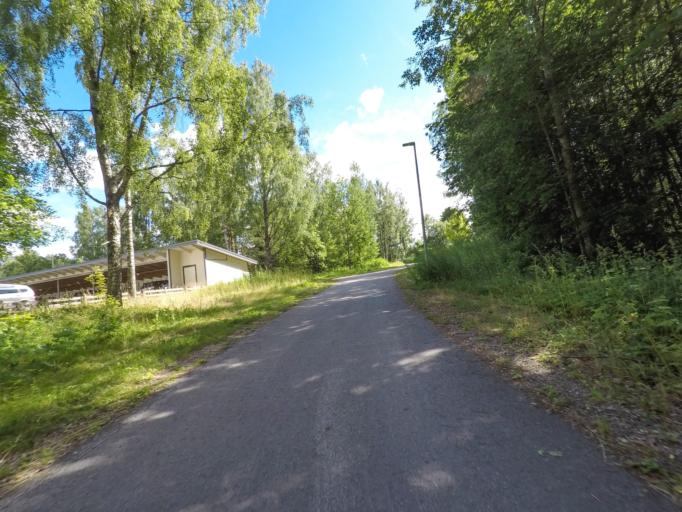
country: FI
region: South Karelia
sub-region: Lappeenranta
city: Lappeenranta
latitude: 61.0629
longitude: 28.2238
